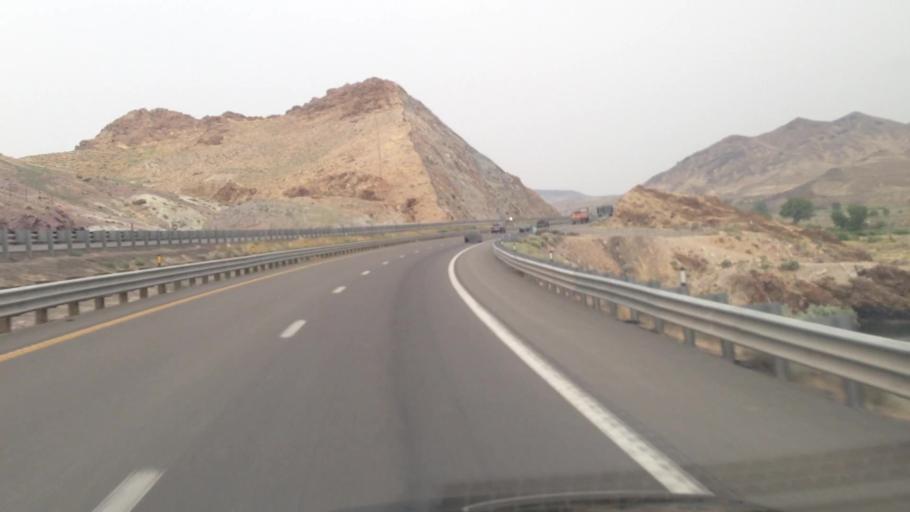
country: US
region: Nevada
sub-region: Lyon County
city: Fernley
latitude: 39.5982
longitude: -119.3585
